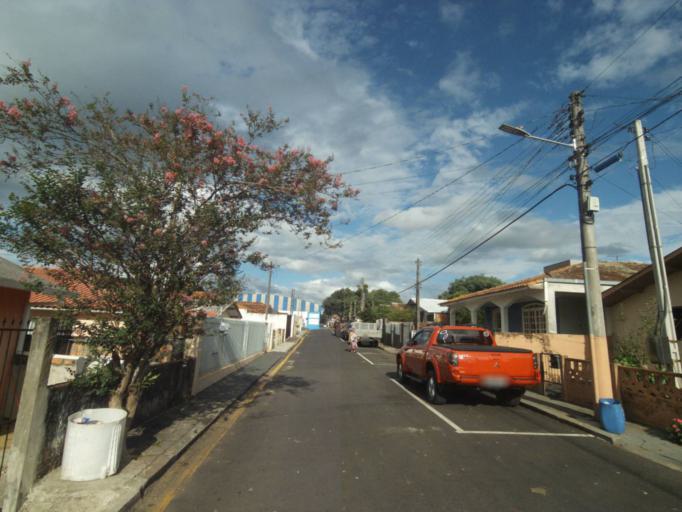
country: BR
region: Parana
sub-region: Telemaco Borba
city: Telemaco Borba
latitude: -24.3356
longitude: -50.6148
